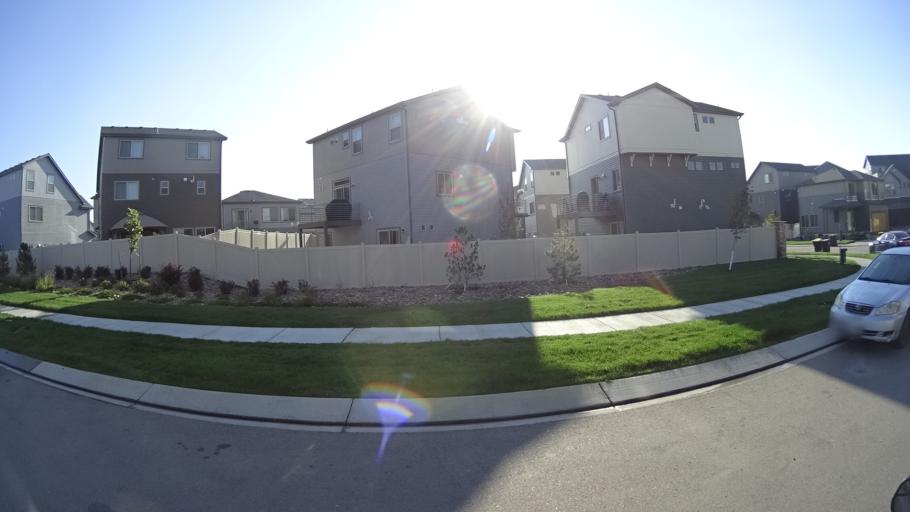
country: US
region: Colorado
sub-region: El Paso County
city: Cimarron Hills
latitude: 38.9274
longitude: -104.6559
